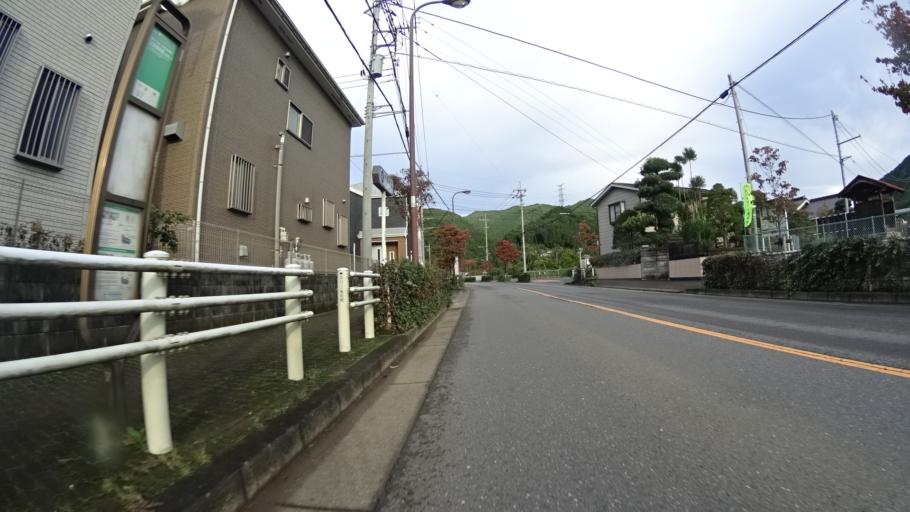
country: JP
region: Tokyo
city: Ome
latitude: 35.8022
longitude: 139.2096
